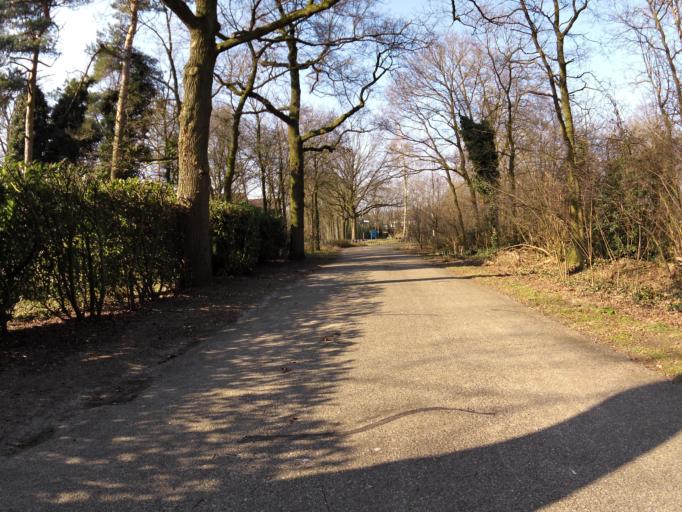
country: NL
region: North Brabant
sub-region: Gemeente Sint-Michielsgestel
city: Sint-Michielsgestel
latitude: 51.7133
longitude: 5.3831
